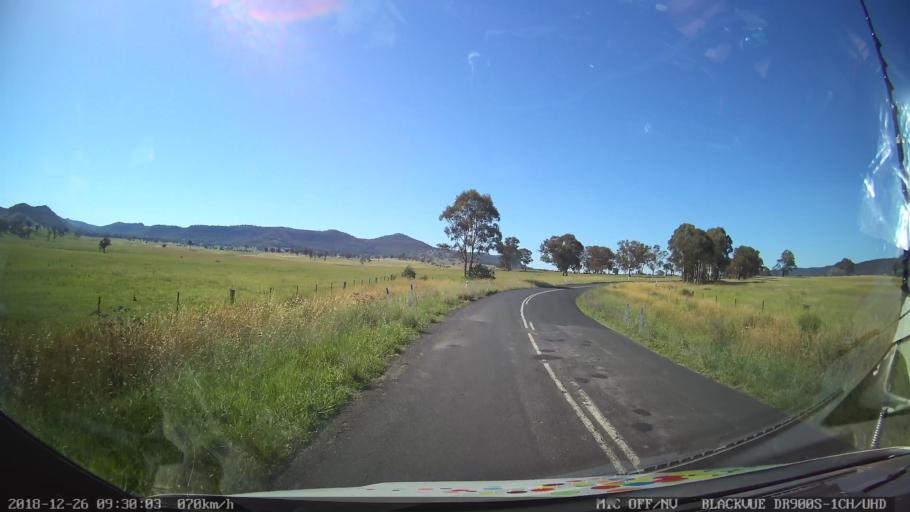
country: AU
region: New South Wales
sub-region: Mid-Western Regional
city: Kandos
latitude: -32.8593
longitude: 150.0303
